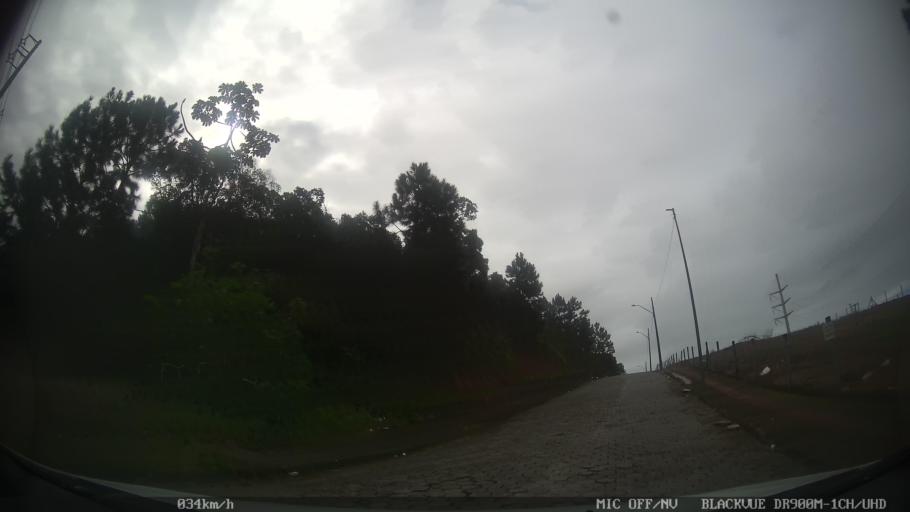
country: BR
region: Santa Catarina
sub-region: Sao Jose
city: Campinas
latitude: -27.5555
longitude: -48.6417
